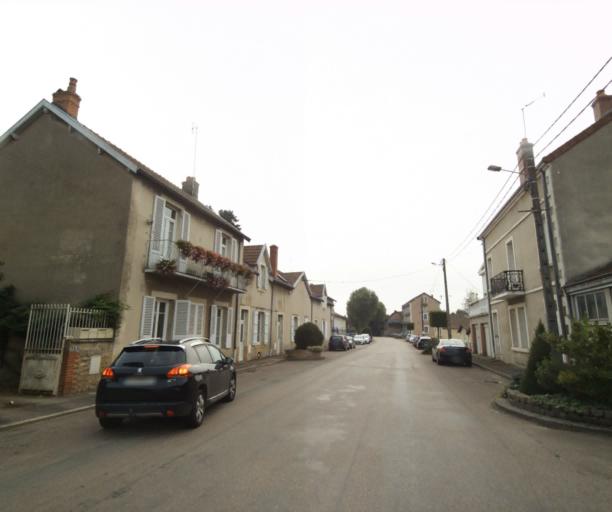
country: FR
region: Bourgogne
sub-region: Departement de Saone-et-Loire
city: Charolles
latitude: 46.4359
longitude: 4.2802
